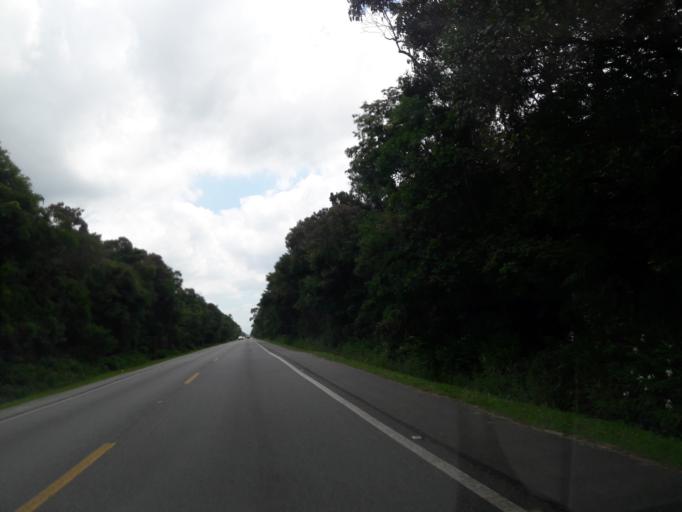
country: BR
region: Parana
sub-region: Pontal Do Parana
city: Pontal do Parana
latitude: -25.6600
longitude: -48.5216
